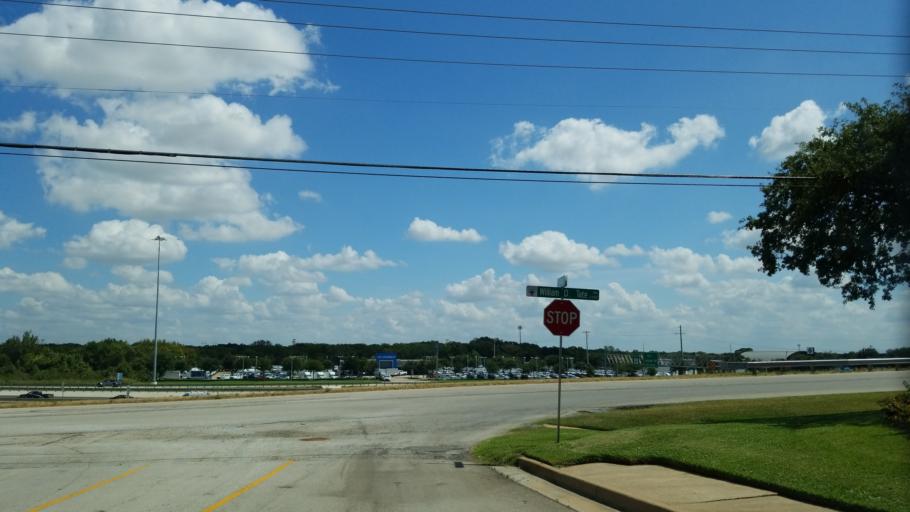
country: US
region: Texas
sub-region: Tarrant County
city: Grapevine
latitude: 32.9120
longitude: -97.0998
